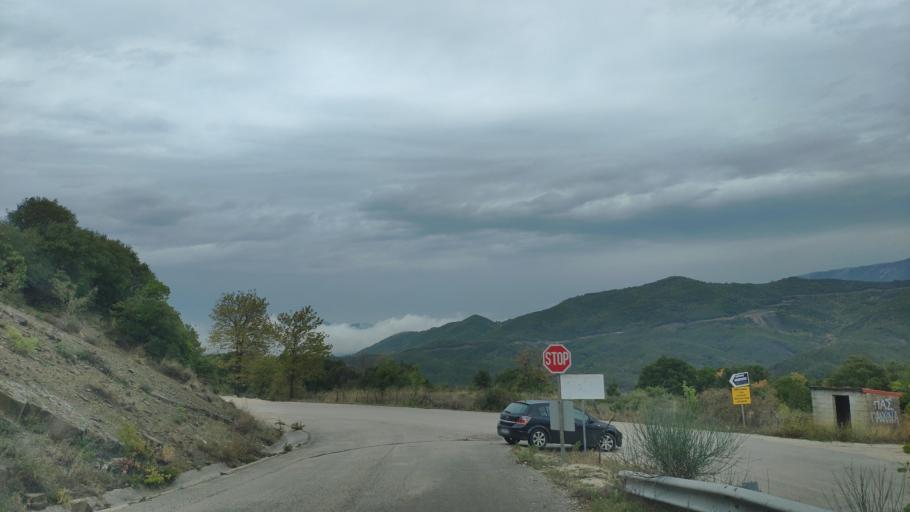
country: GR
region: Epirus
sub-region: Nomos Thesprotias
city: Paramythia
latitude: 39.4584
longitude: 20.6787
